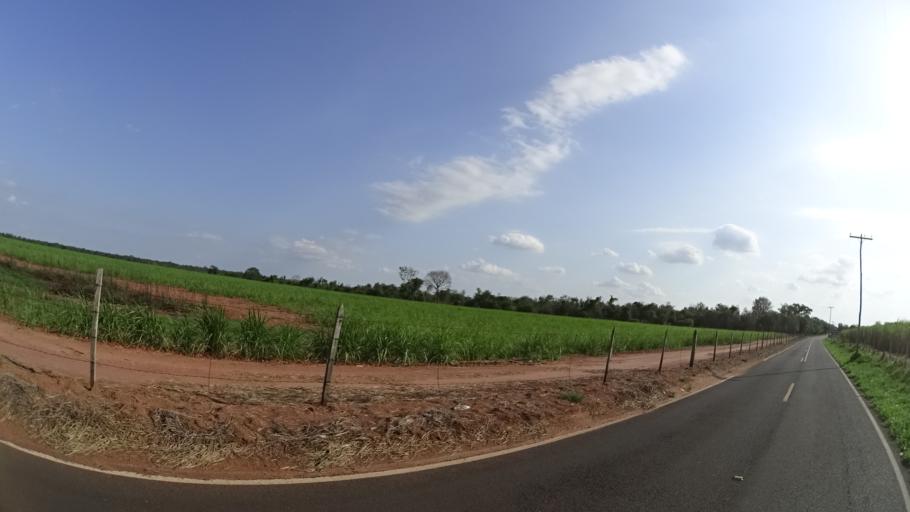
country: BR
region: Sao Paulo
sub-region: Urupes
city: Urupes
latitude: -21.3933
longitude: -49.5080
